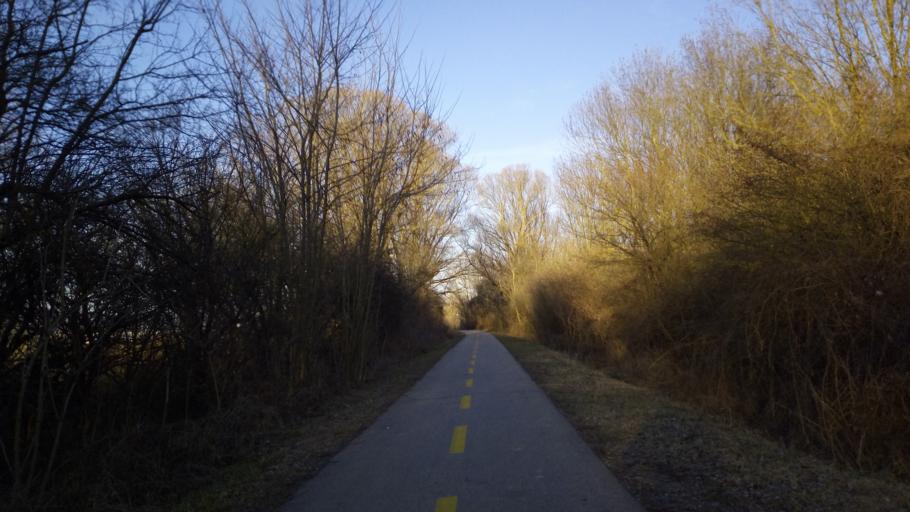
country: HU
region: Baranya
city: Pellerd
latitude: 46.0432
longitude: 18.1839
